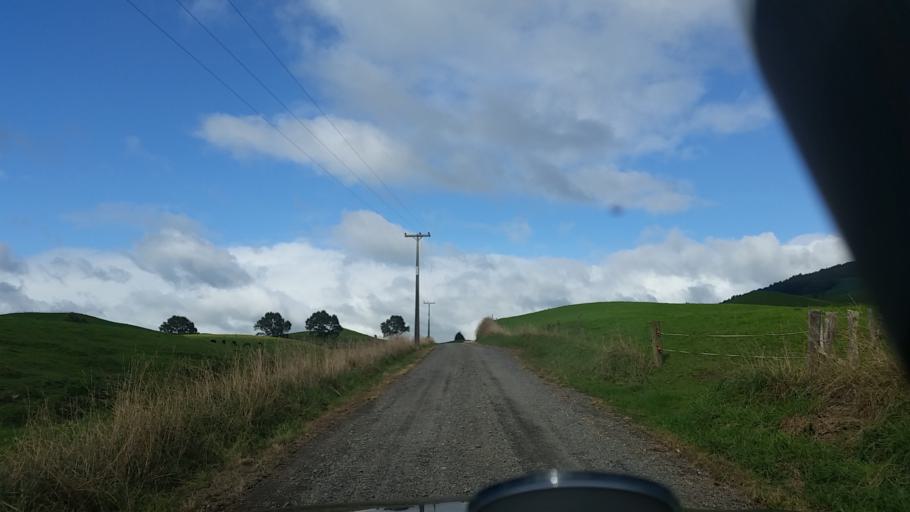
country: NZ
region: Waikato
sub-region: Matamata-Piako District
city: Matamata
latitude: -37.8165
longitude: 175.6736
